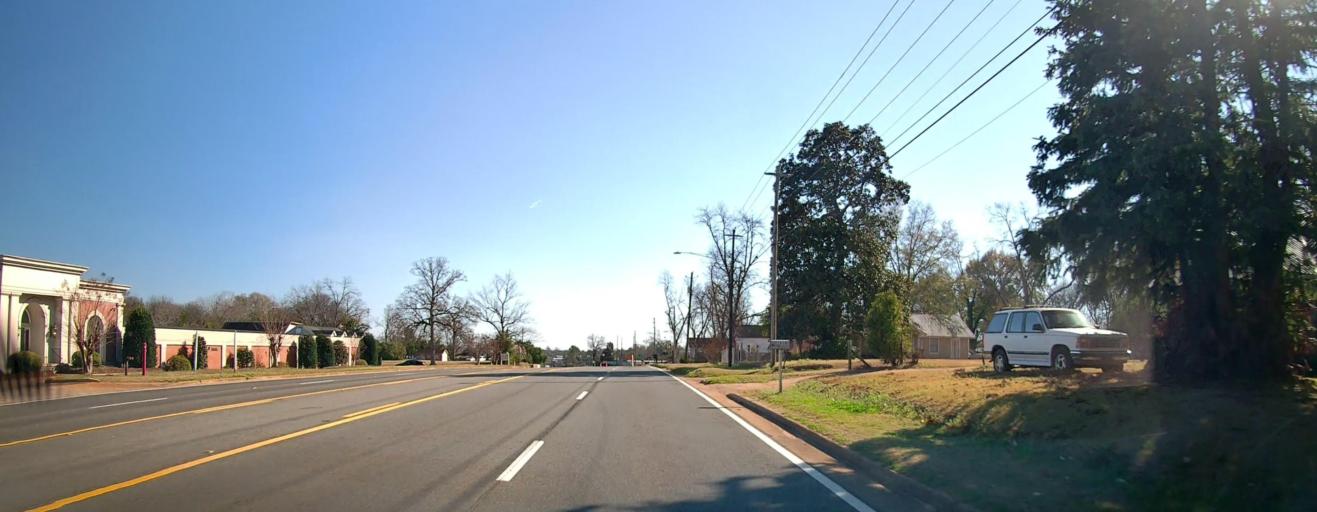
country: US
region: Georgia
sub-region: Sumter County
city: Americus
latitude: 32.0886
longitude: -84.2404
